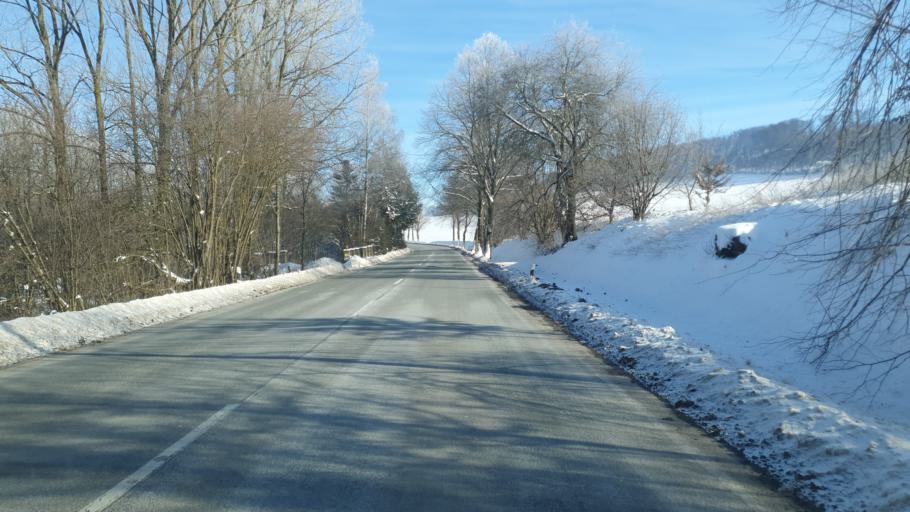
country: DE
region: Lower Saxony
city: Bad Pyrmont
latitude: 52.0174
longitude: 9.2175
